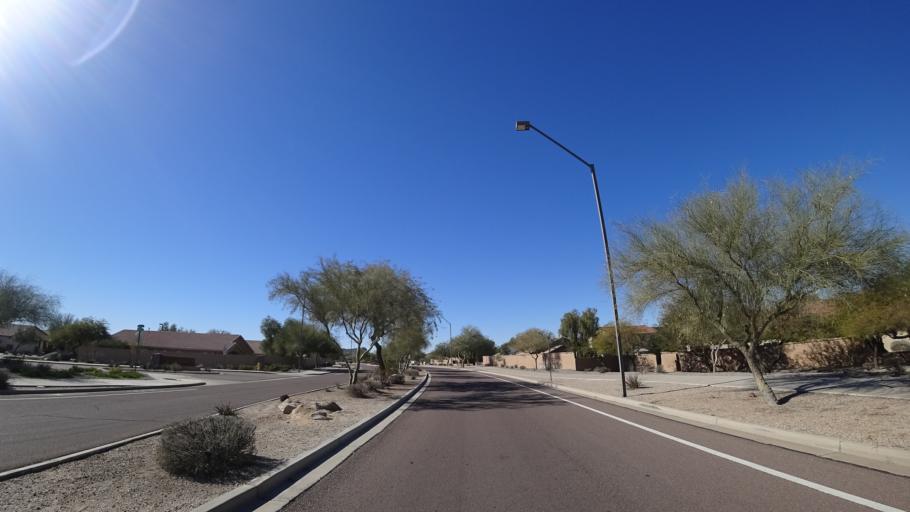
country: US
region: Arizona
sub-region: Maricopa County
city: Goodyear
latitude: 33.3323
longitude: -112.4259
